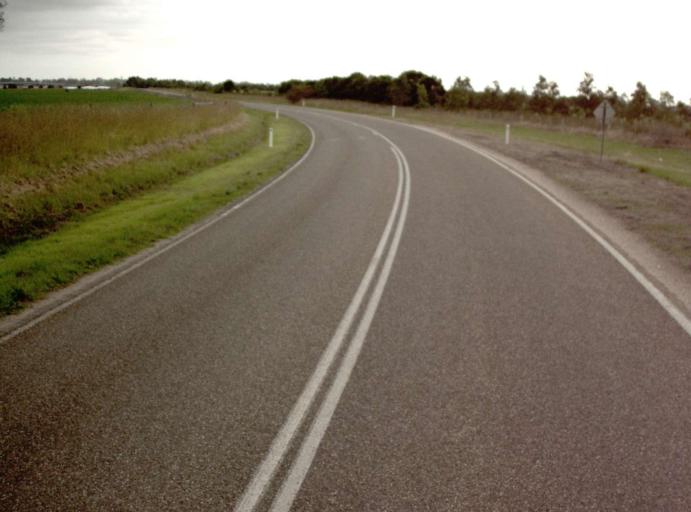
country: AU
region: Victoria
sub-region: Wellington
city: Sale
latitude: -37.8431
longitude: 147.0558
